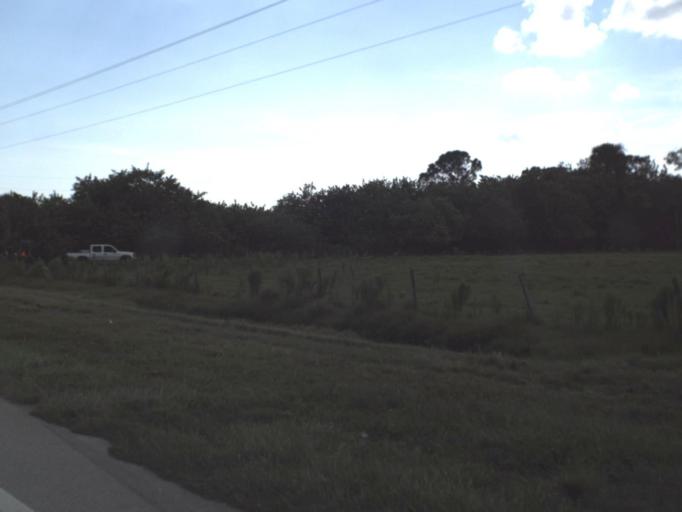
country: US
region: Florida
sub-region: Okeechobee County
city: Okeechobee
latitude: 27.2935
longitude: -80.8892
